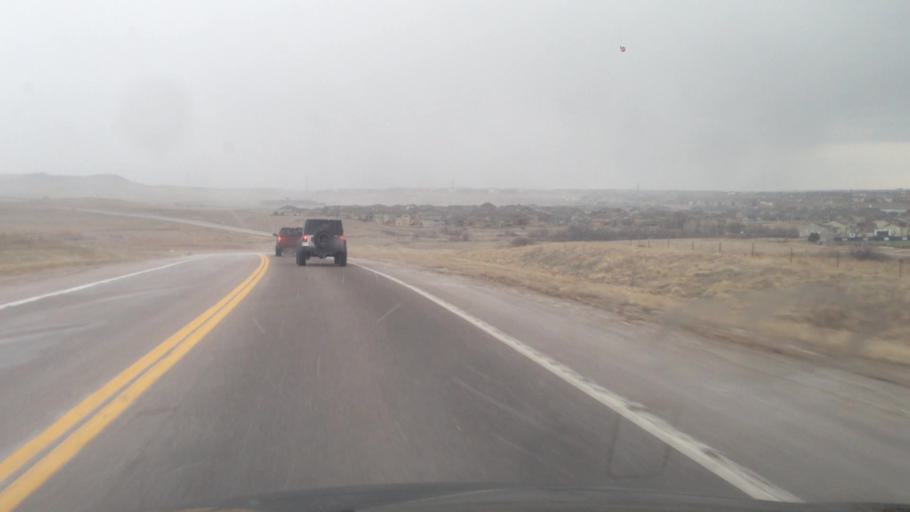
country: US
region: Colorado
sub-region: Douglas County
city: Stonegate
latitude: 39.4942
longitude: -104.8144
